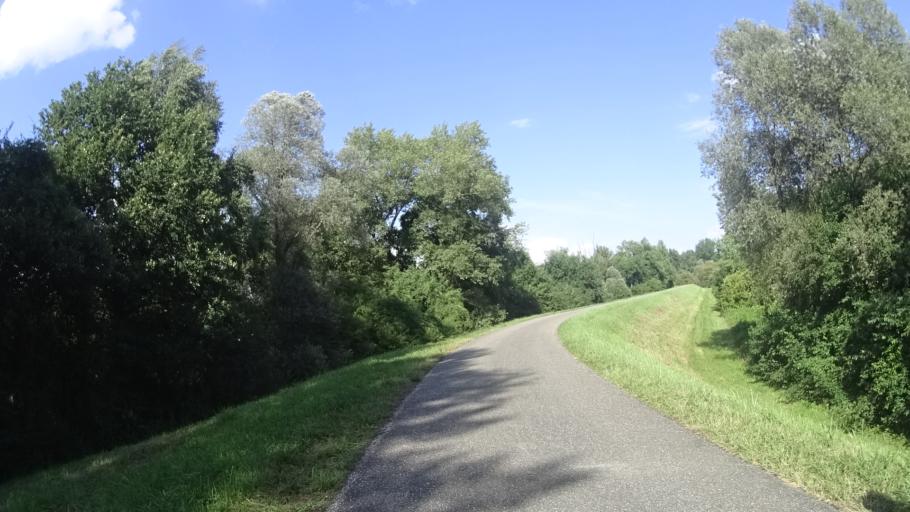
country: FR
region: Alsace
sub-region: Departement du Bas-Rhin
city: Seltz
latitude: 48.8734
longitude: 8.1109
